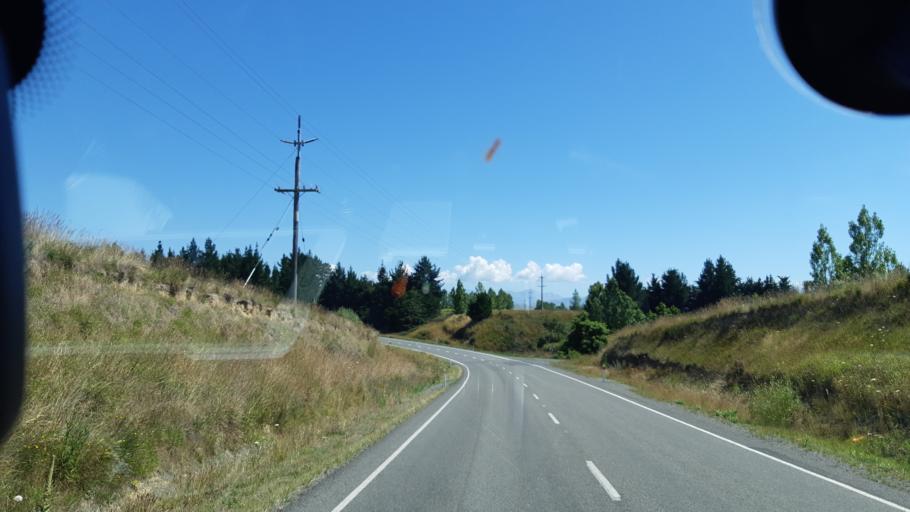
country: NZ
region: Canterbury
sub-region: Kaikoura District
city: Kaikoura
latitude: -42.7534
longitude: 173.2732
